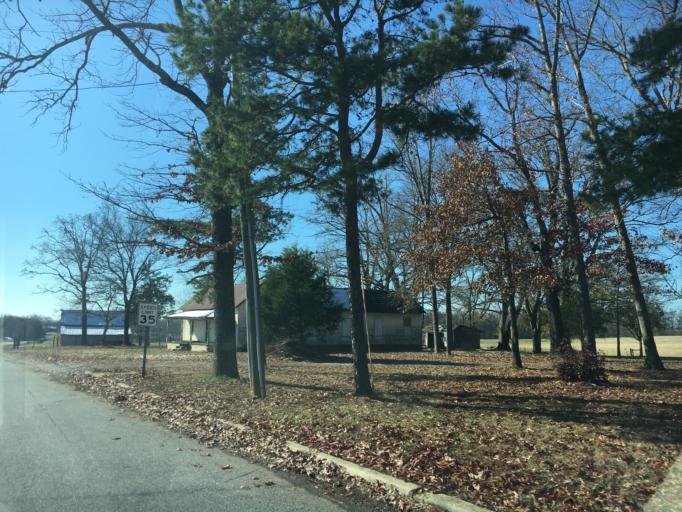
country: US
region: South Carolina
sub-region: Greenville County
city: Greer
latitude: 34.9020
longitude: -82.2377
